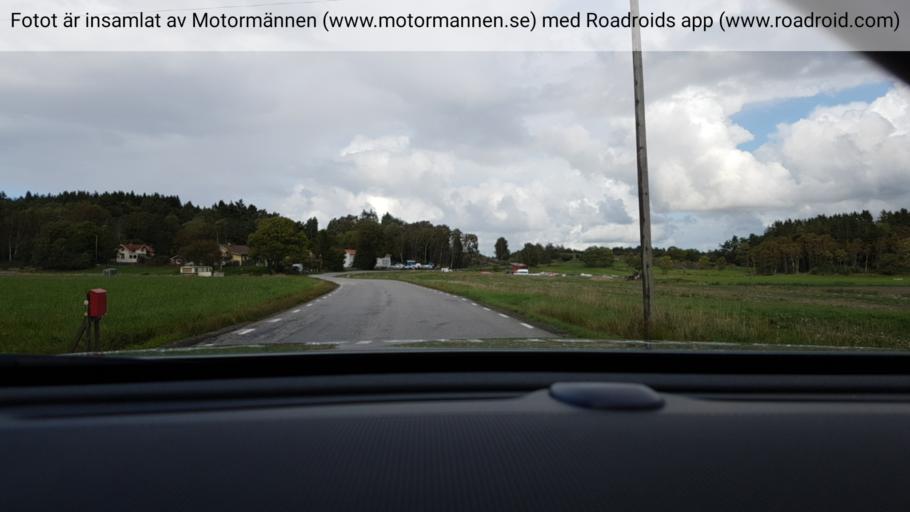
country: SE
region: Vaestra Goetaland
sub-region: Orust
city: Henan
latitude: 58.1570
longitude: 11.5959
